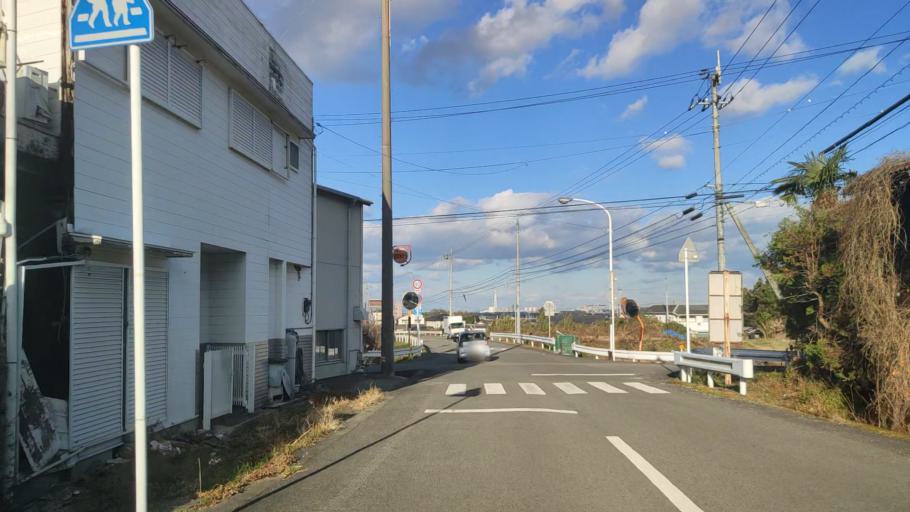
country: JP
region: Ehime
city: Saijo
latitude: 33.8893
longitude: 133.1306
